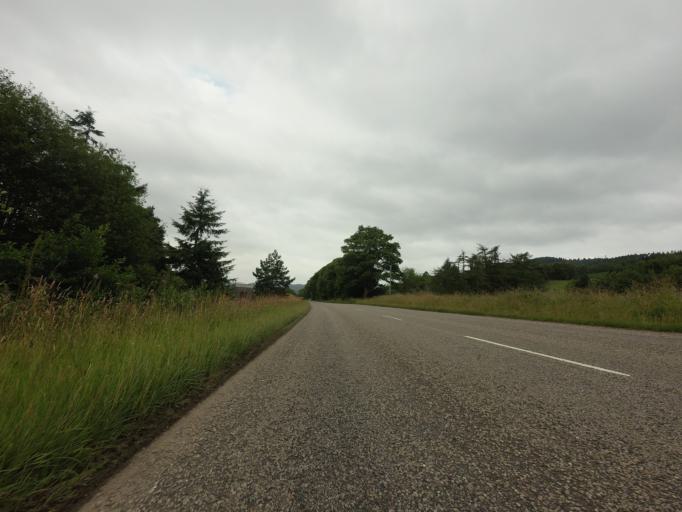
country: GB
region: Scotland
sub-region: Highland
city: Alness
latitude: 57.9113
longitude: -4.3741
